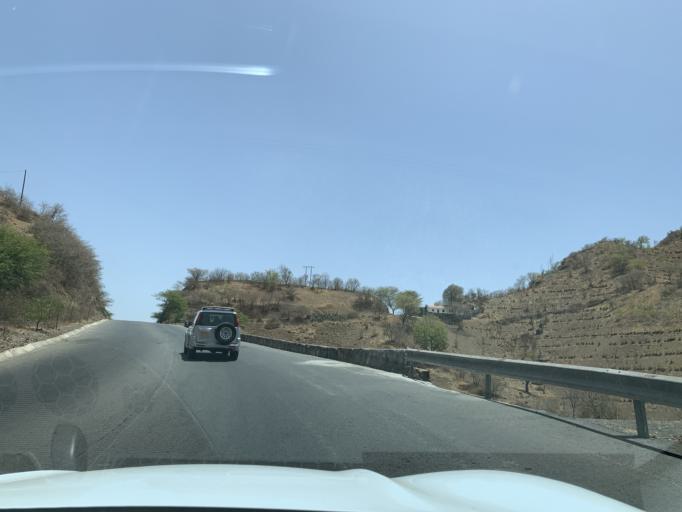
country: CV
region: Sao Domingos
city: Sao Domingos
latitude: 15.0444
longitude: -23.5760
